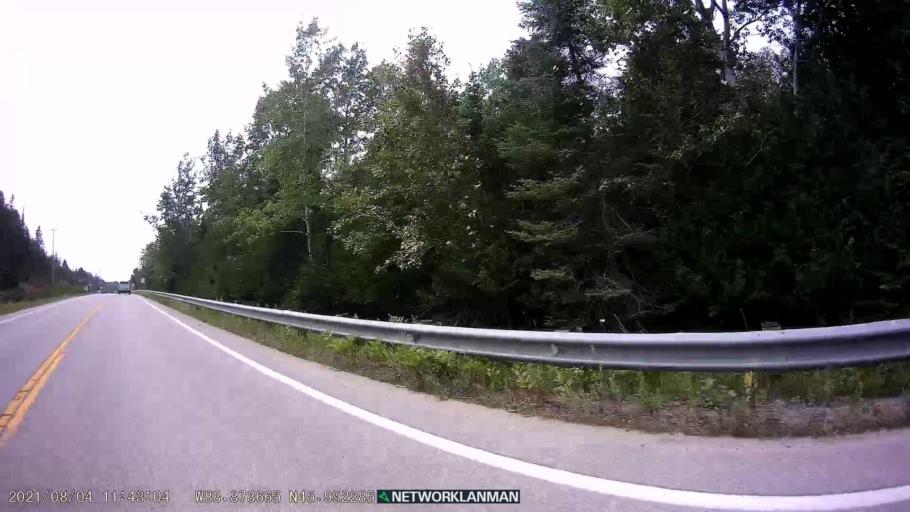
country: CA
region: Ontario
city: Thessalon
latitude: 45.9919
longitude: -83.8740
